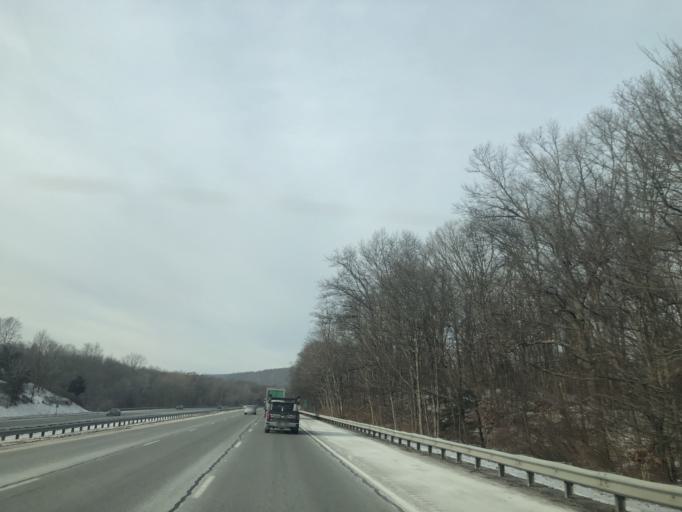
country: US
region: New Jersey
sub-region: Sussex County
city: Stanhope
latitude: 40.9122
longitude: -74.7520
